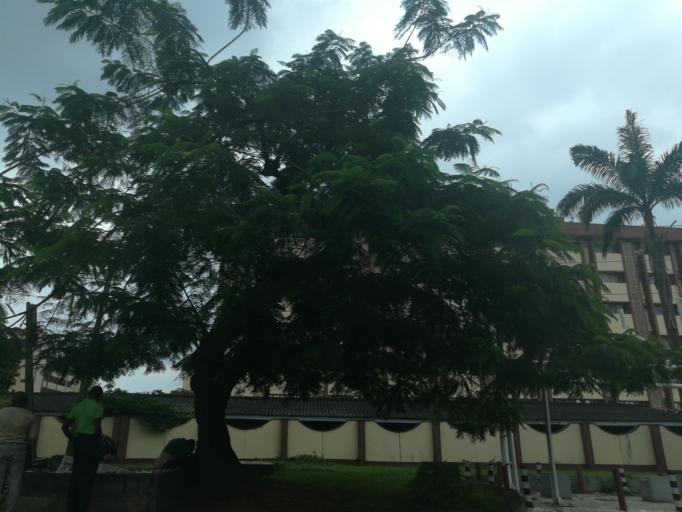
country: NG
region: Lagos
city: Ikeja
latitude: 6.6174
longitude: 3.3601
